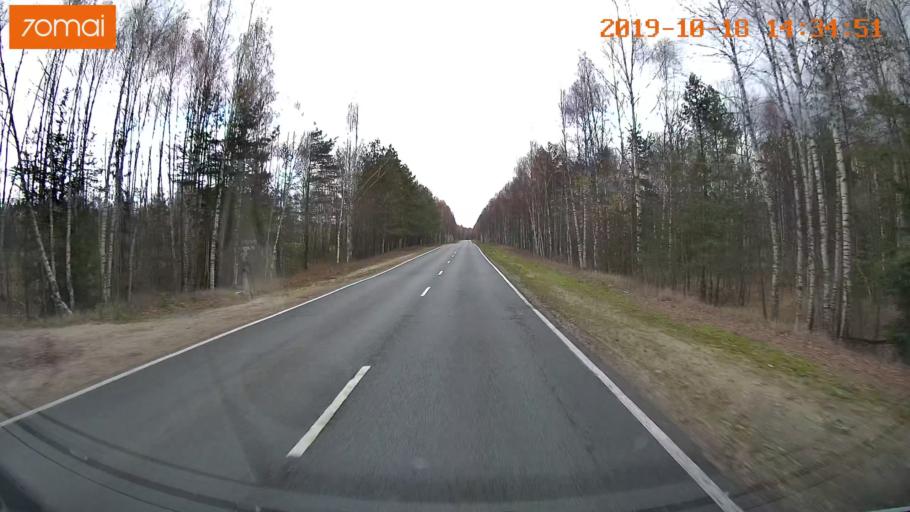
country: RU
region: Vladimir
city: Velikodvorskiy
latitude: 55.2167
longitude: 40.6243
